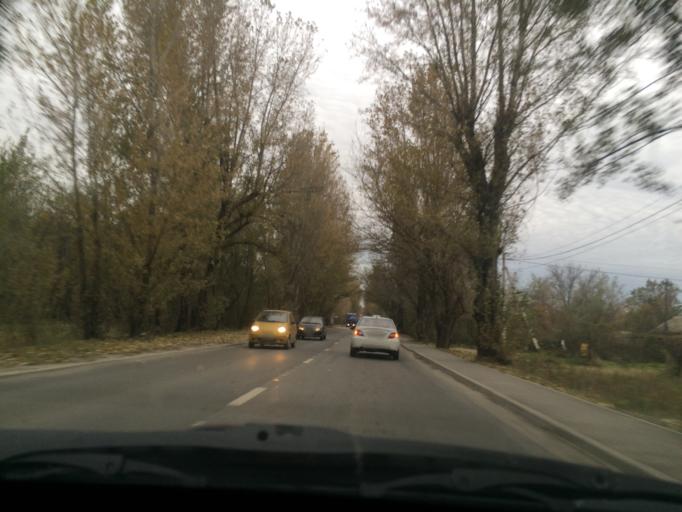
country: RU
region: Rostov
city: Severnyy
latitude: 47.2870
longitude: 39.6618
